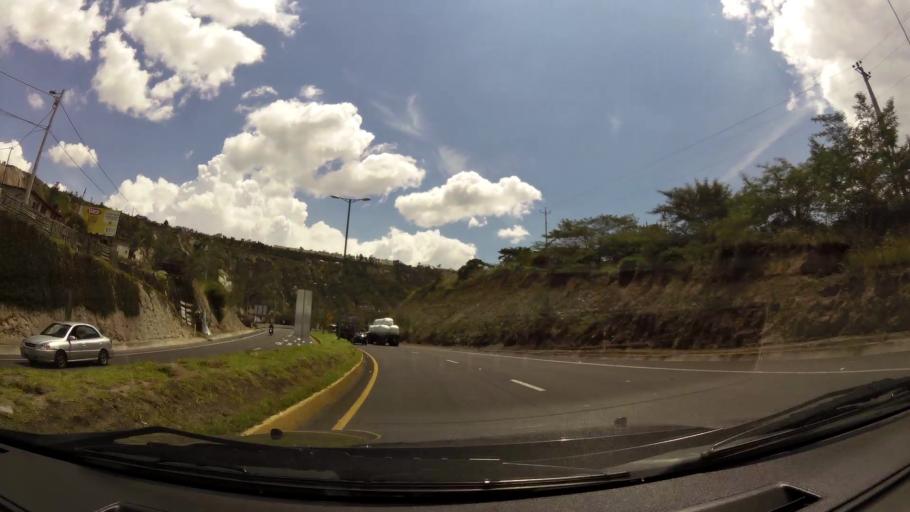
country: EC
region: Pichincha
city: Quito
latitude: -0.1008
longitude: -78.4126
